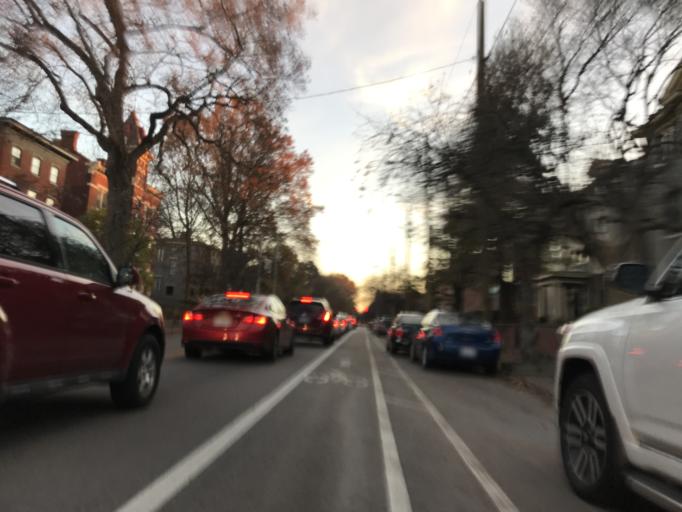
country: US
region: Kentucky
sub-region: Jefferson County
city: Louisville
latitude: 38.2363
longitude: -85.7551
